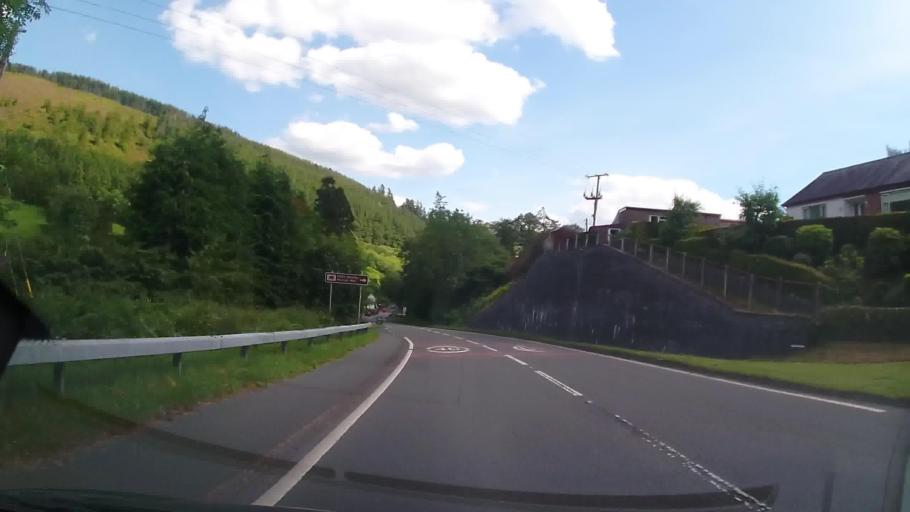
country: GB
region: Wales
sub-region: Gwynedd
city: Corris
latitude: 52.7128
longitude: -3.6909
